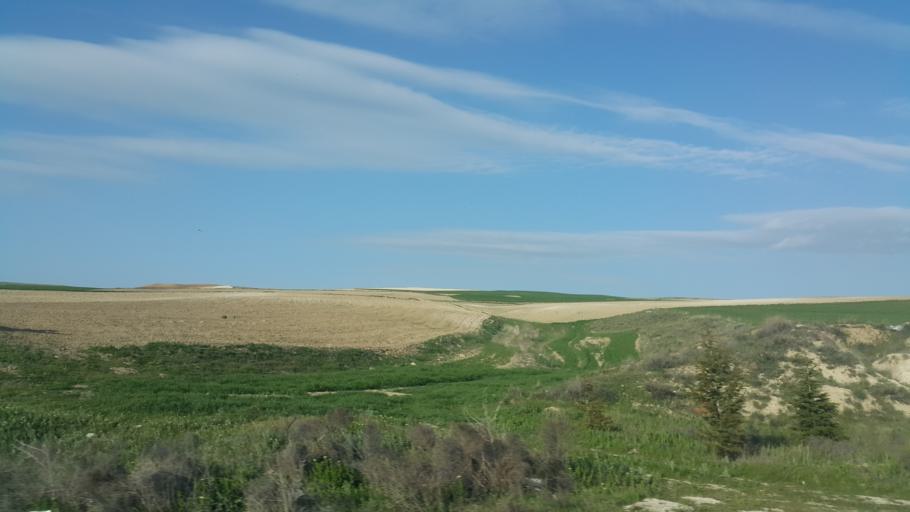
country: TR
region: Ankara
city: Sereflikochisar
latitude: 39.0636
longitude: 33.4245
